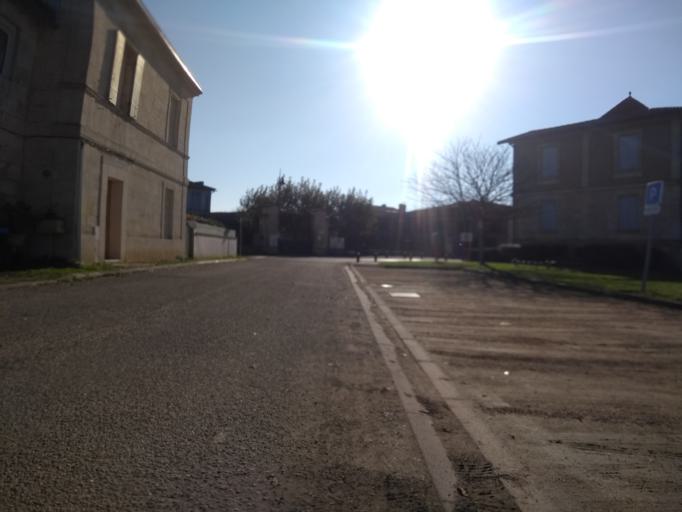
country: FR
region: Aquitaine
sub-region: Departement de la Gironde
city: Cambes
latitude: 44.7251
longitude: -0.4716
